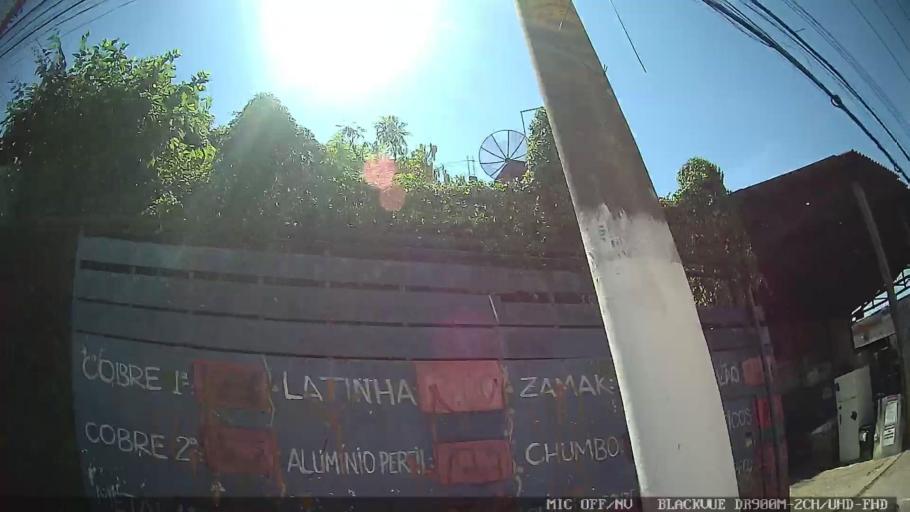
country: BR
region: Sao Paulo
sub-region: Sao Caetano Do Sul
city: Sao Caetano do Sul
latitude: -23.5972
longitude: -46.5073
